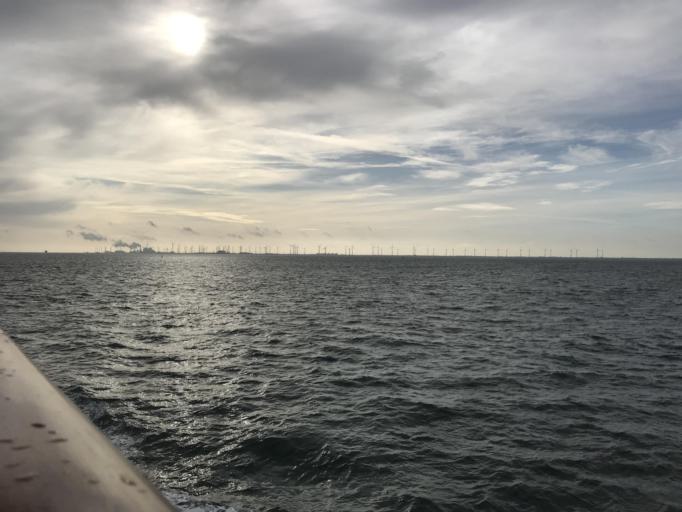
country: DE
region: Lower Saxony
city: Borkum
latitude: 53.5260
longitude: 6.7657
